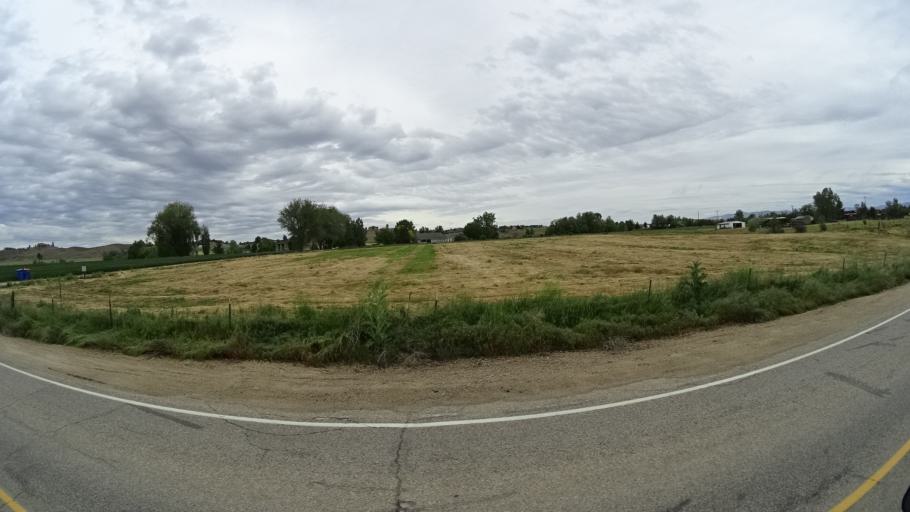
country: US
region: Idaho
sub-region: Ada County
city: Star
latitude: 43.7211
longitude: -116.4754
